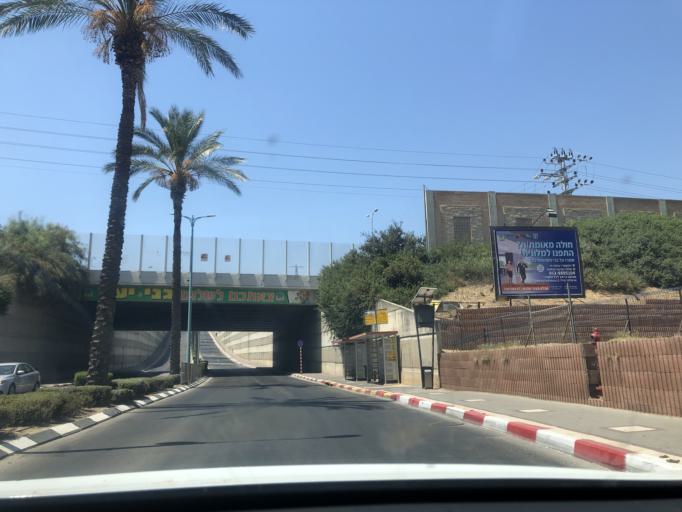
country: IL
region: Central District
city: Lod
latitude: 31.9465
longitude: 34.9048
